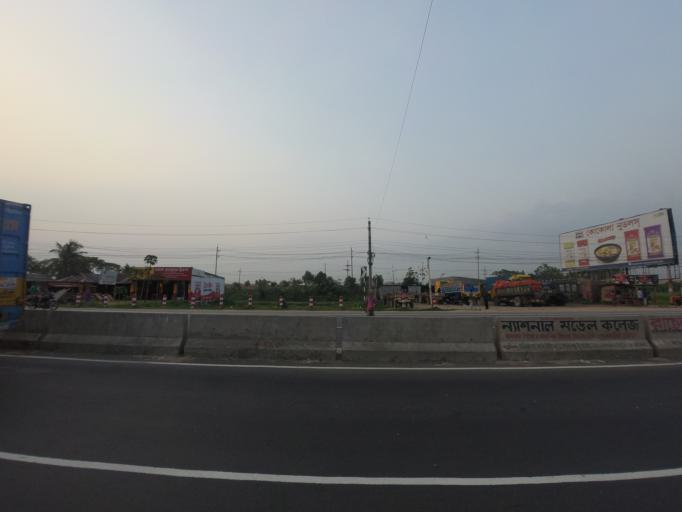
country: BD
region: Chittagong
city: Comilla
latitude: 23.4800
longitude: 91.1280
